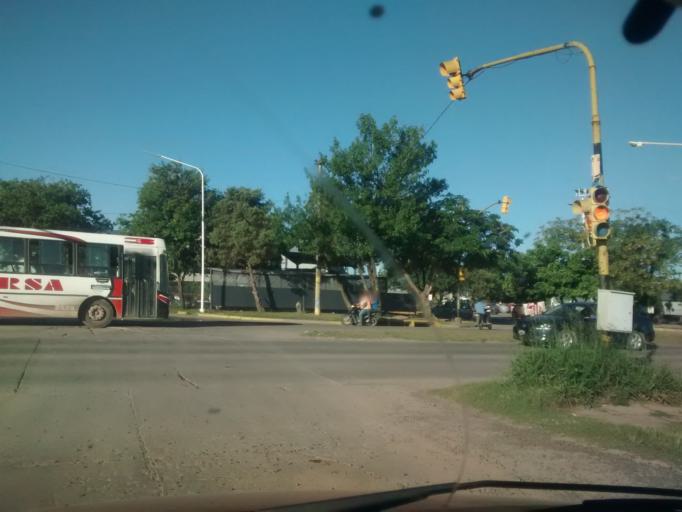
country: AR
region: Chaco
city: Fontana
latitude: -27.4570
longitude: -59.0234
